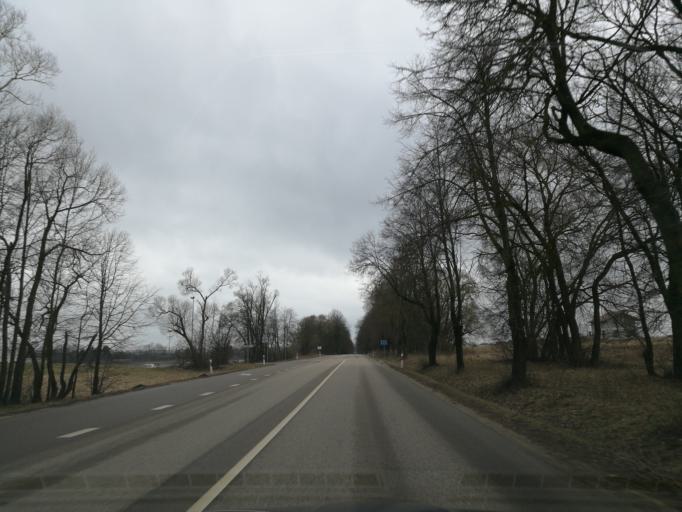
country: LT
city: Lentvaris
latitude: 54.6437
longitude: 25.0814
